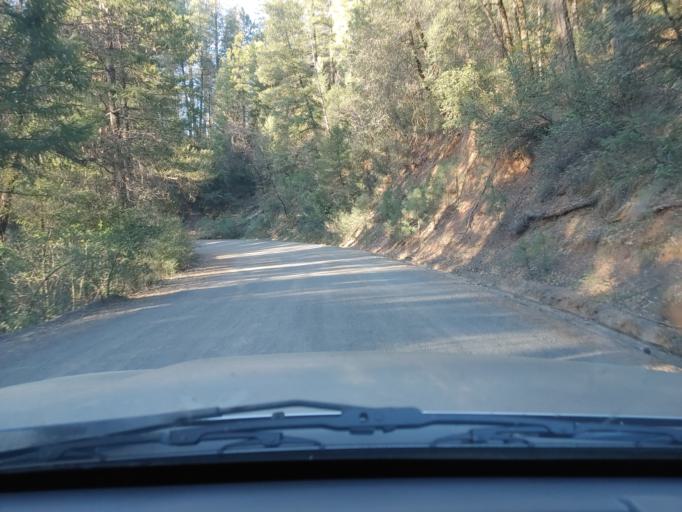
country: US
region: California
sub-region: Shasta County
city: Bella Vista
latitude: 40.8229
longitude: -122.0175
